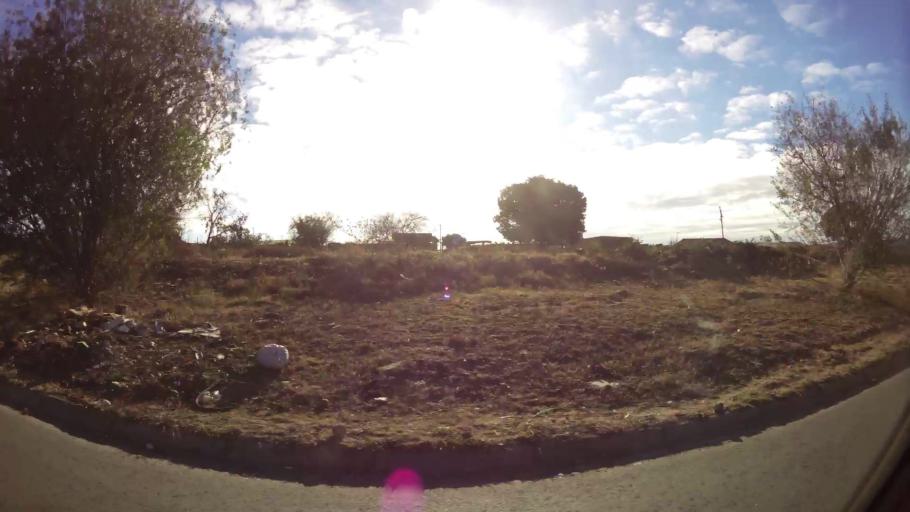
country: ZA
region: Gauteng
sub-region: City of Johannesburg Metropolitan Municipality
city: Modderfontein
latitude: -26.0528
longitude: 28.1776
